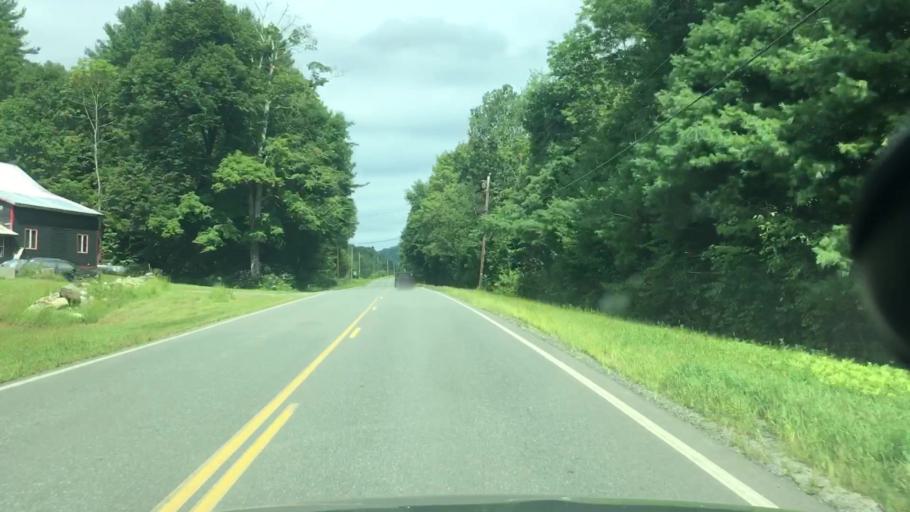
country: US
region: Massachusetts
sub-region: Franklin County
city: Colrain
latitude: 42.7181
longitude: -72.7070
